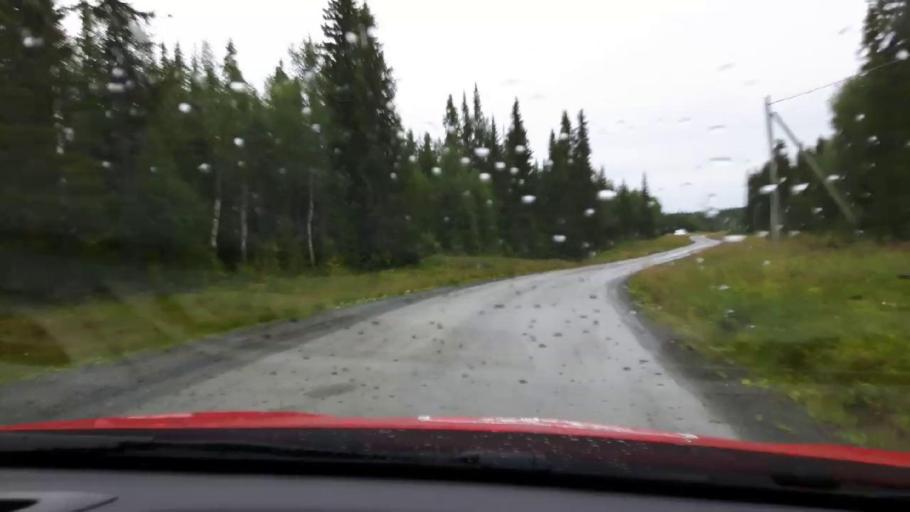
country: SE
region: Jaemtland
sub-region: Are Kommun
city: Are
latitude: 63.4431
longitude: 12.8081
